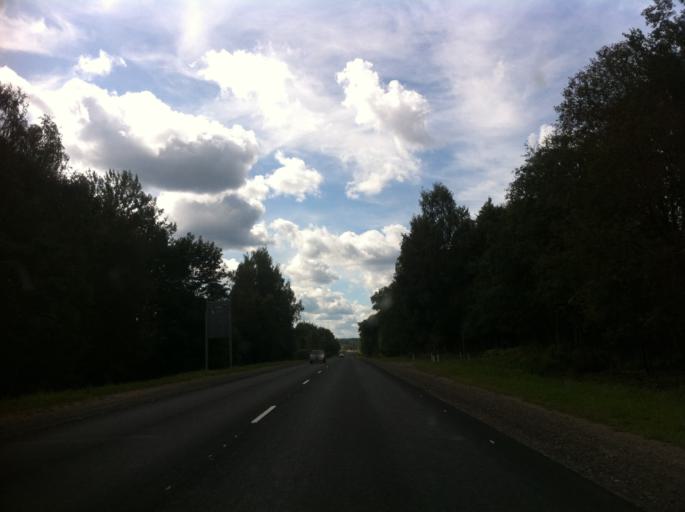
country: RU
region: Pskov
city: Izborsk
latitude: 57.7105
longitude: 27.8956
